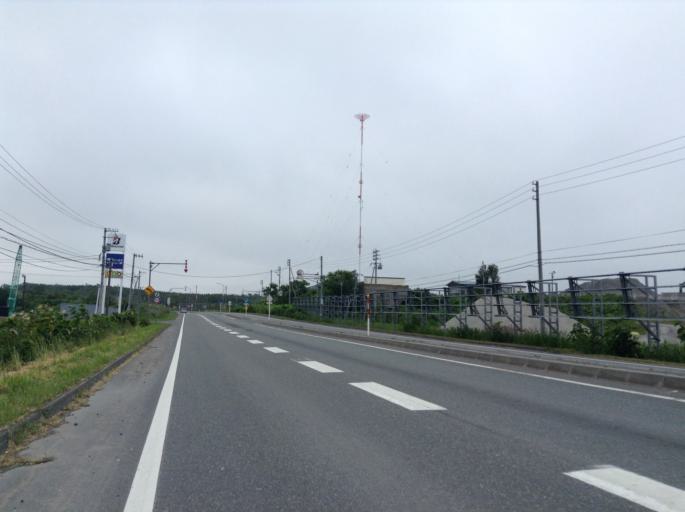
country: JP
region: Hokkaido
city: Wakkanai
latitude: 45.3780
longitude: 141.7112
